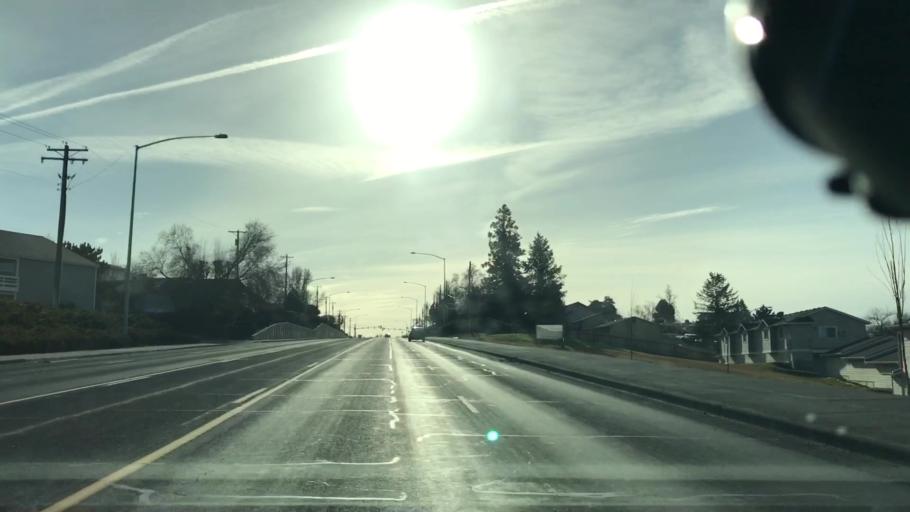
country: US
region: Washington
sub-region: Grant County
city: Moses Lake
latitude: 47.1249
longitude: -119.2686
